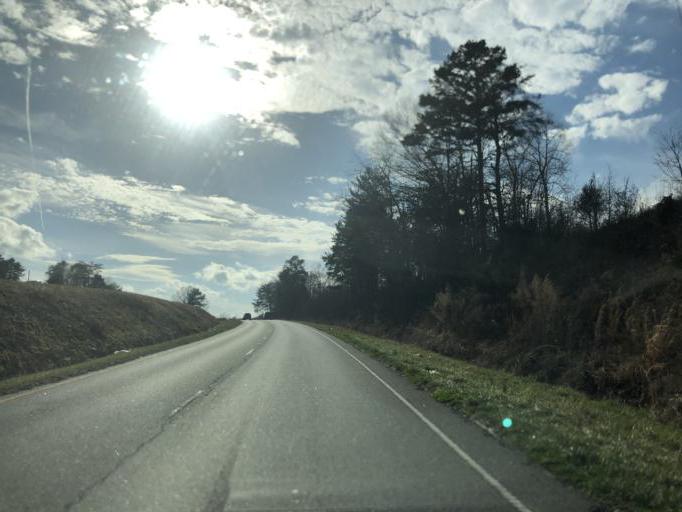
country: US
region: North Carolina
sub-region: Gaston County
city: Bessemer City
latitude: 35.2540
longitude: -81.2760
